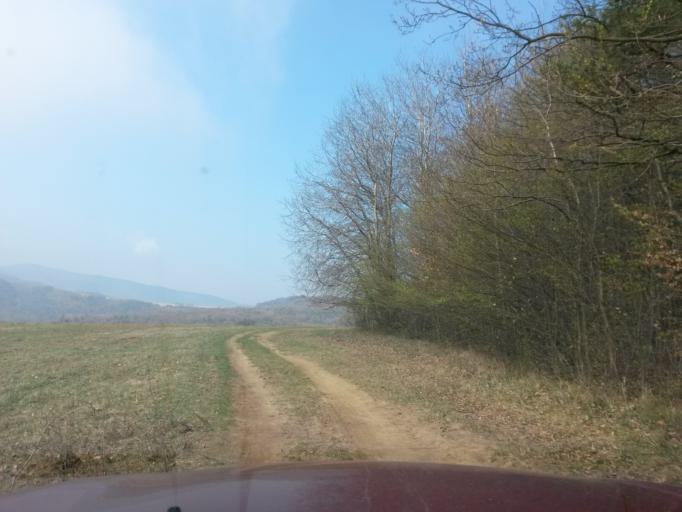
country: SK
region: Presovsky
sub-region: Okres Presov
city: Presov
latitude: 48.9222
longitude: 21.1689
